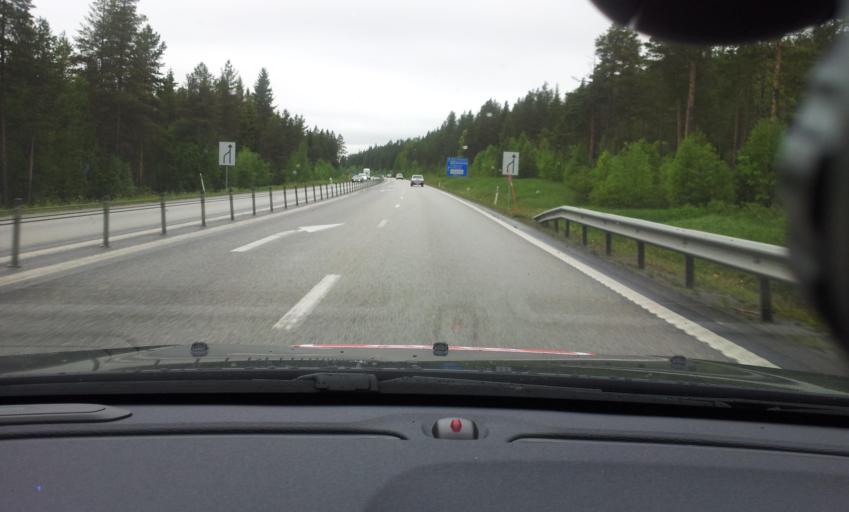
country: SE
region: Jaemtland
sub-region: OEstersunds Kommun
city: Ostersund
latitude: 63.1937
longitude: 14.6893
